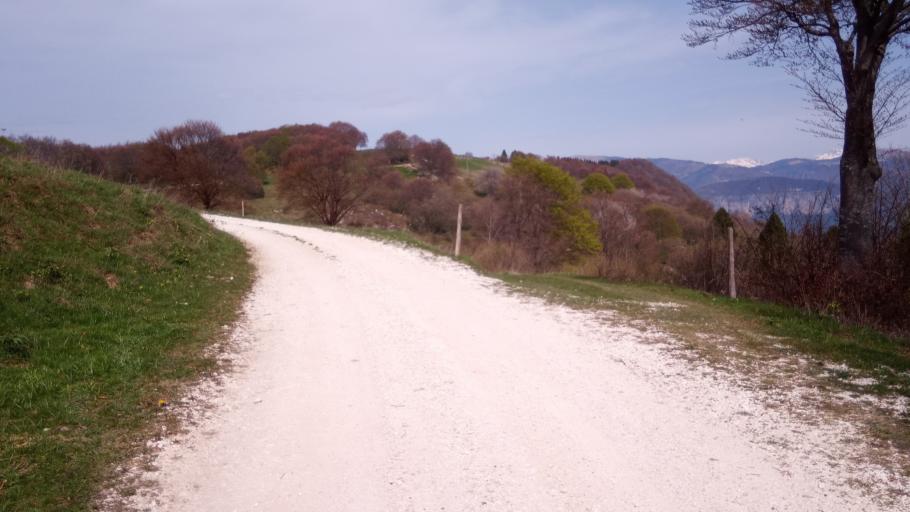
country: IT
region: Veneto
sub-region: Provincia di Vicenza
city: Campolongo sul Brenta
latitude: 45.8158
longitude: 11.6802
